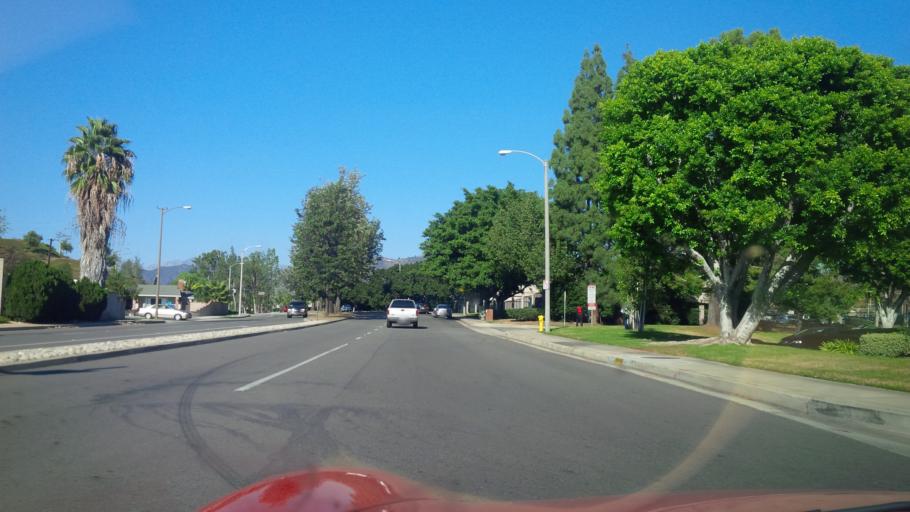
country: US
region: California
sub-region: Los Angeles County
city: Charter Oak
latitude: 34.1079
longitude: -117.8285
